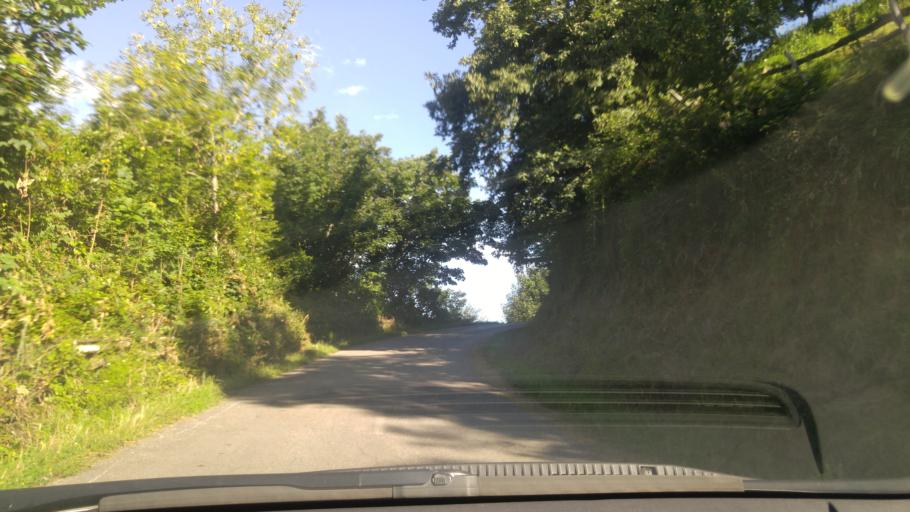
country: ES
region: Asturias
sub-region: Province of Asturias
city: Barzana
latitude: 43.1727
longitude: -5.9852
